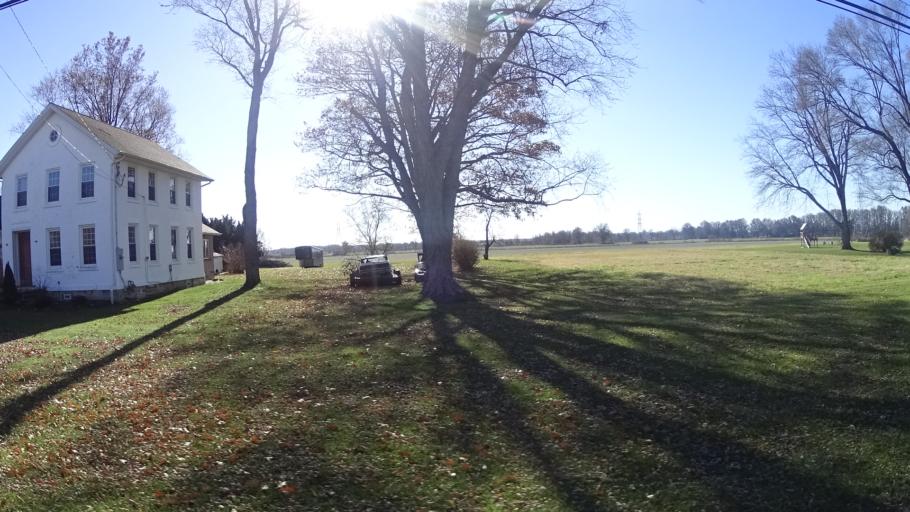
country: US
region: Ohio
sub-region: Lorain County
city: Elyria
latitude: 41.3753
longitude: -82.1532
